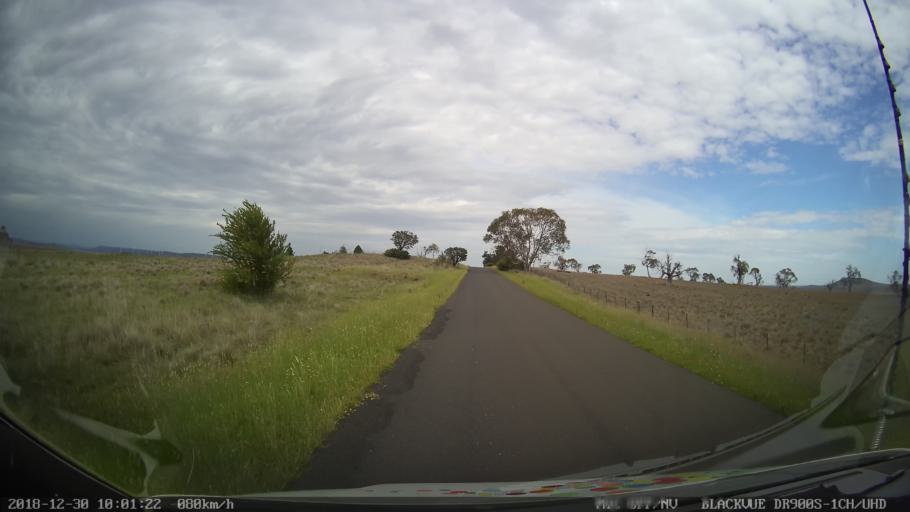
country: AU
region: New South Wales
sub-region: Cooma-Monaro
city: Cooma
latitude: -36.5153
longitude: 149.1868
